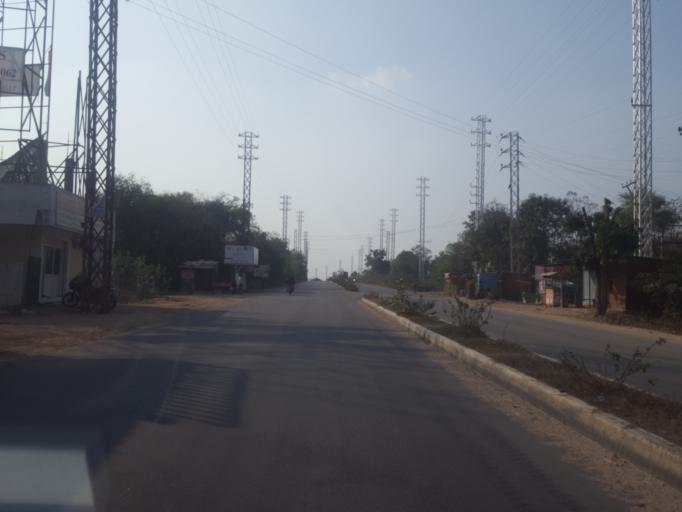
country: IN
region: Telangana
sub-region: Medak
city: Serilingampalle
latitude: 17.4175
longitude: 78.2512
